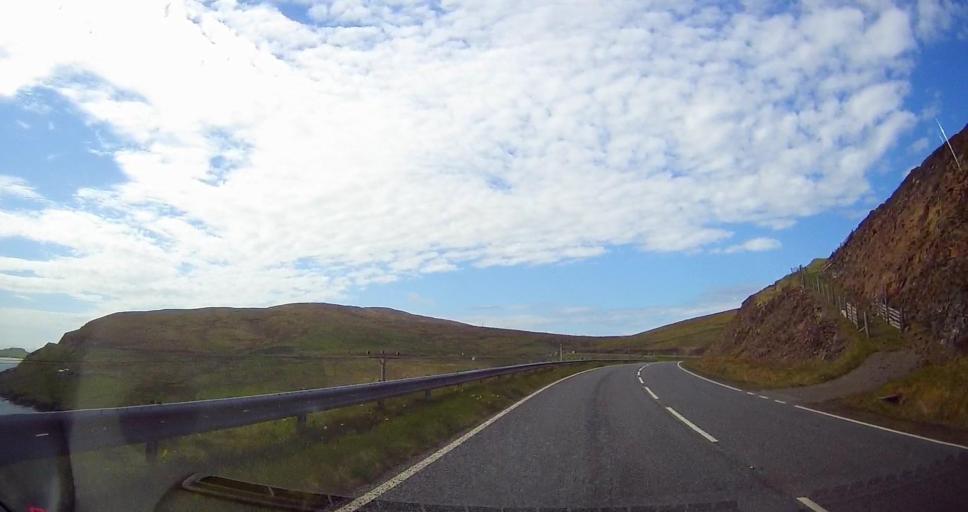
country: GB
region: Scotland
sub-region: Shetland Islands
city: Sandwick
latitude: 59.9936
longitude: -1.2787
